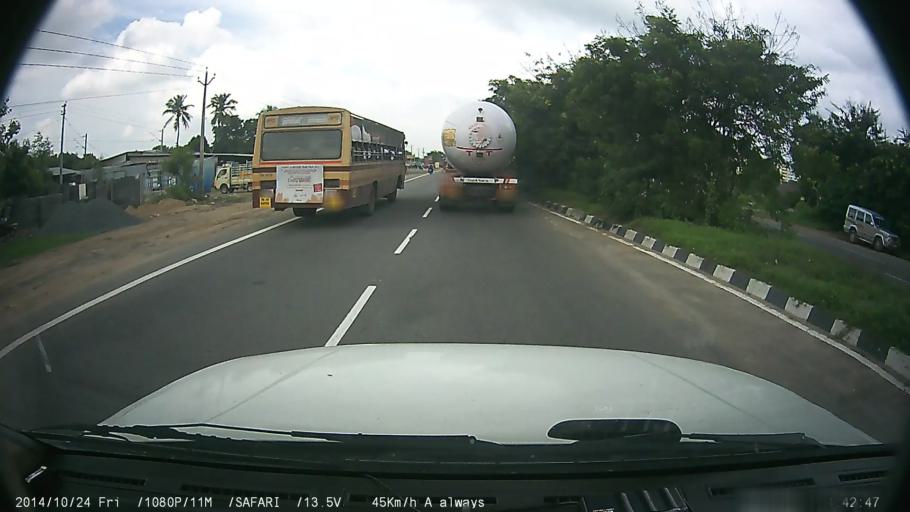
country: IN
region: Tamil Nadu
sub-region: Kancheepuram
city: Singapperumalkovil
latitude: 12.7706
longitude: 80.0075
